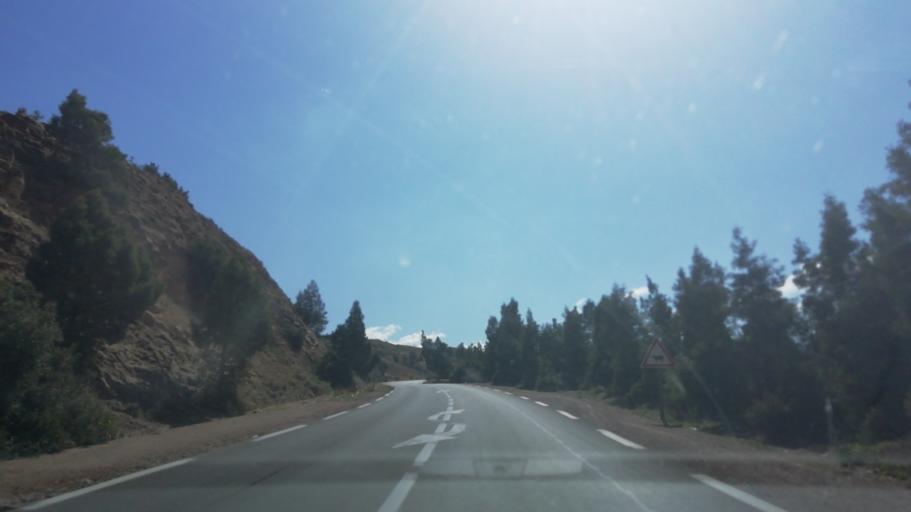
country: DZ
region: Mascara
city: Mascara
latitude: 35.4966
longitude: 0.1332
